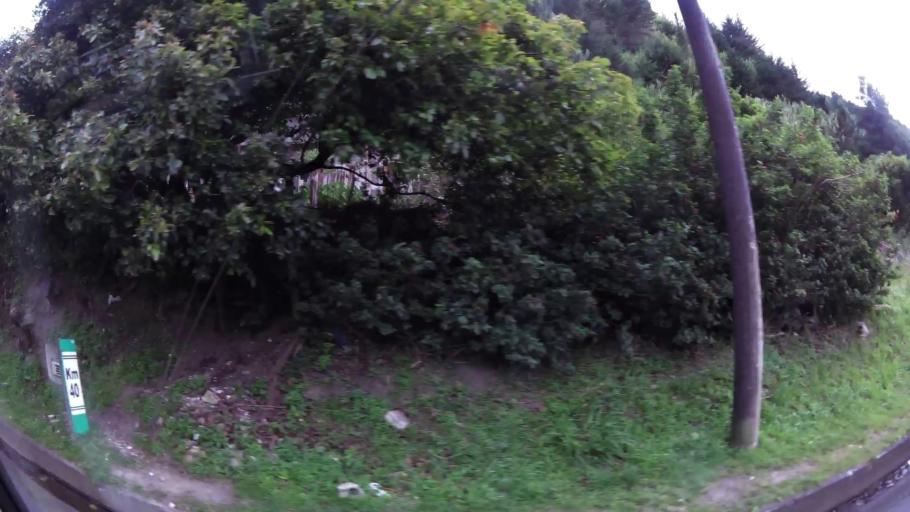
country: EC
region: Tungurahua
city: Banos
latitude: -1.3951
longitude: -78.3898
